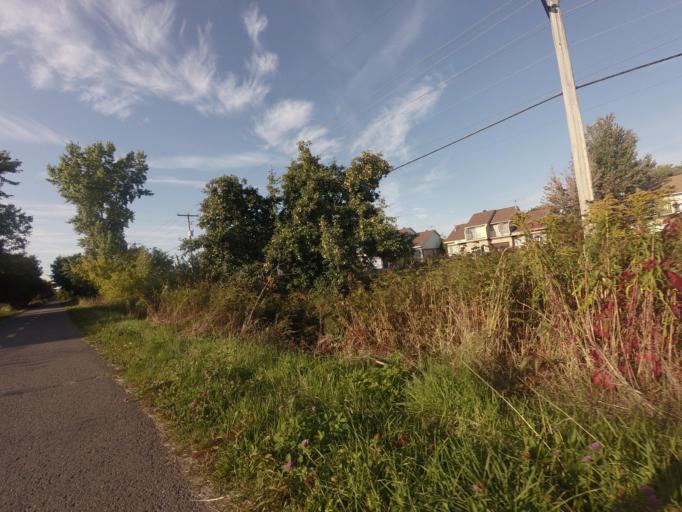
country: CA
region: Quebec
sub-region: Laurentides
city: Saint-Jerome
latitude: 45.7984
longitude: -74.0036
